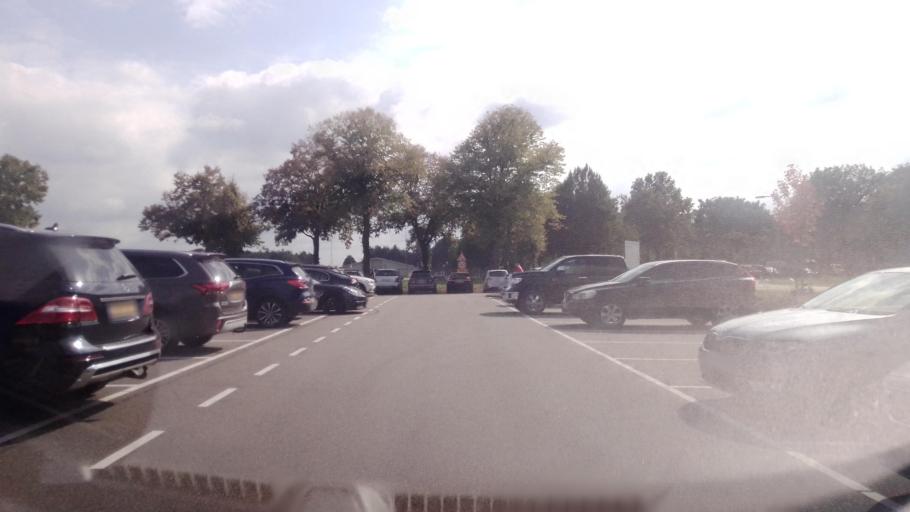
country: NL
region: Limburg
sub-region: Gemeente Peel en Maas
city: Maasbree
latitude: 51.4107
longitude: 5.9683
